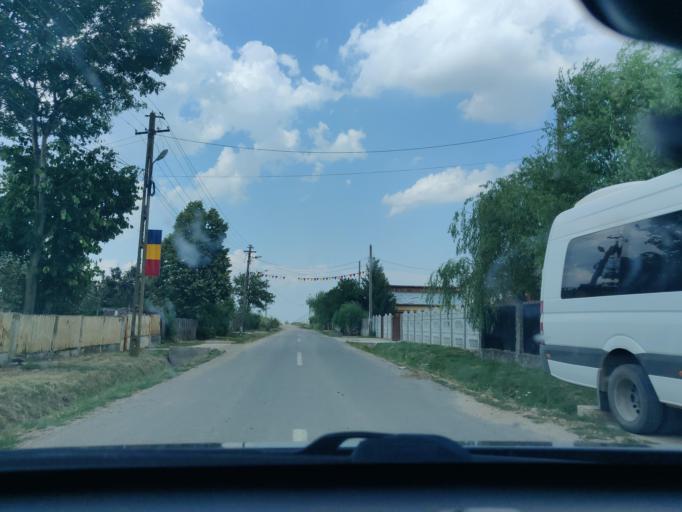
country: RO
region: Teleorman
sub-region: Comuna Sarbeni
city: Sarbeni
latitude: 44.4793
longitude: 25.3872
